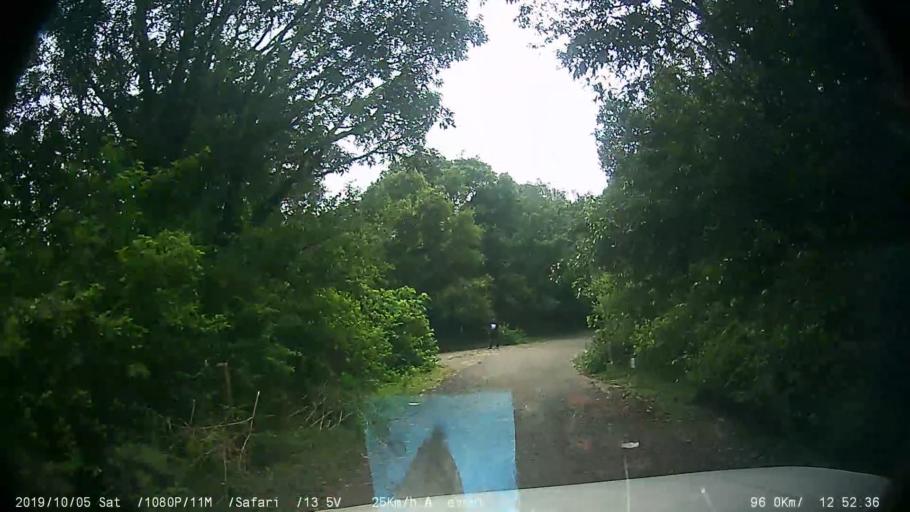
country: IN
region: Kerala
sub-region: Kottayam
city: Erattupetta
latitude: 9.5733
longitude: 76.9707
